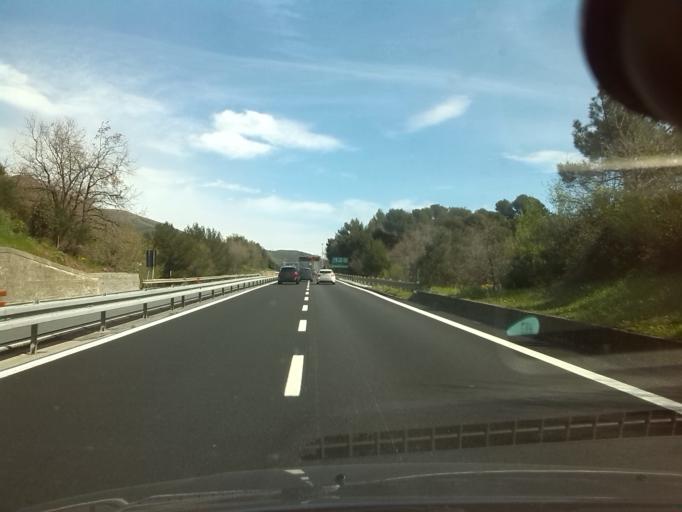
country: IT
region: Liguria
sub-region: Provincia di Savona
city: Campochiesa
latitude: 44.0839
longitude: 8.2001
